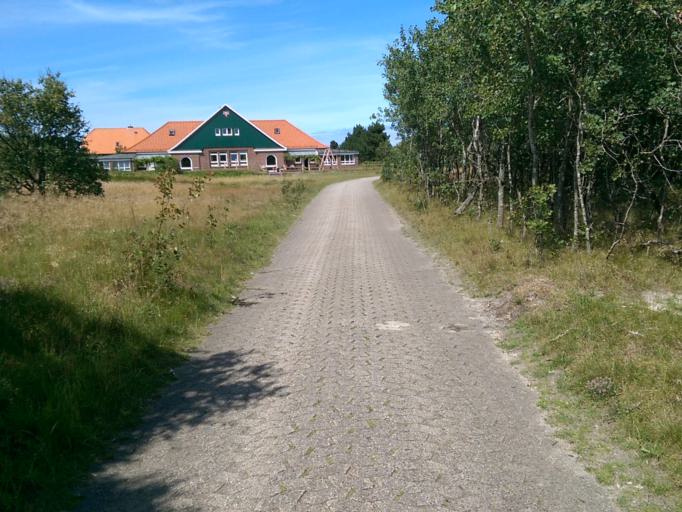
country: DE
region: Lower Saxony
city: Spiekeroog
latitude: 53.7703
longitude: 7.7239
